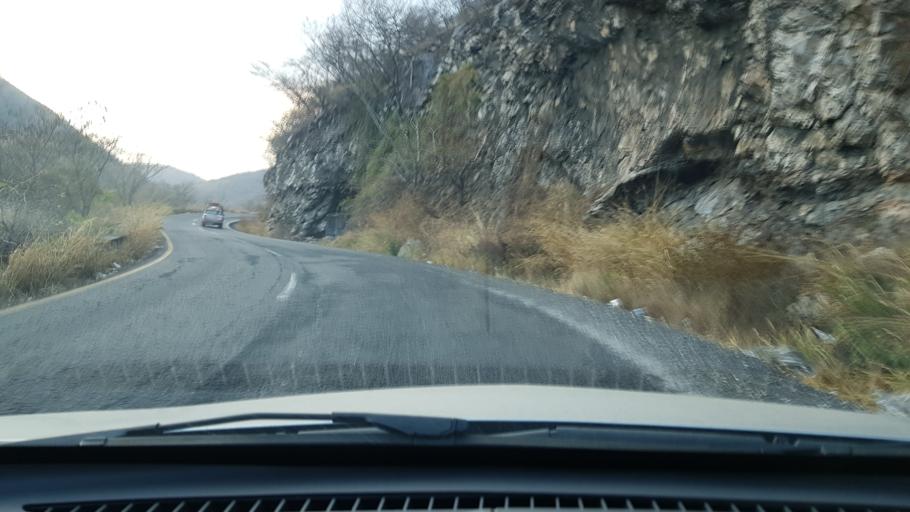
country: MX
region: Morelos
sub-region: Jiutepec
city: Independencia
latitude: 18.8612
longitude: -99.1206
